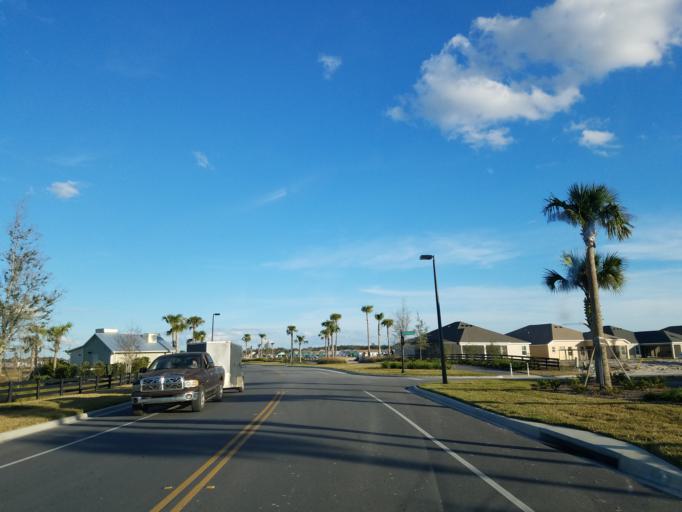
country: US
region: Florida
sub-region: Sumter County
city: Lake Panasoffkee
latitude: 28.7934
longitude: -82.0339
